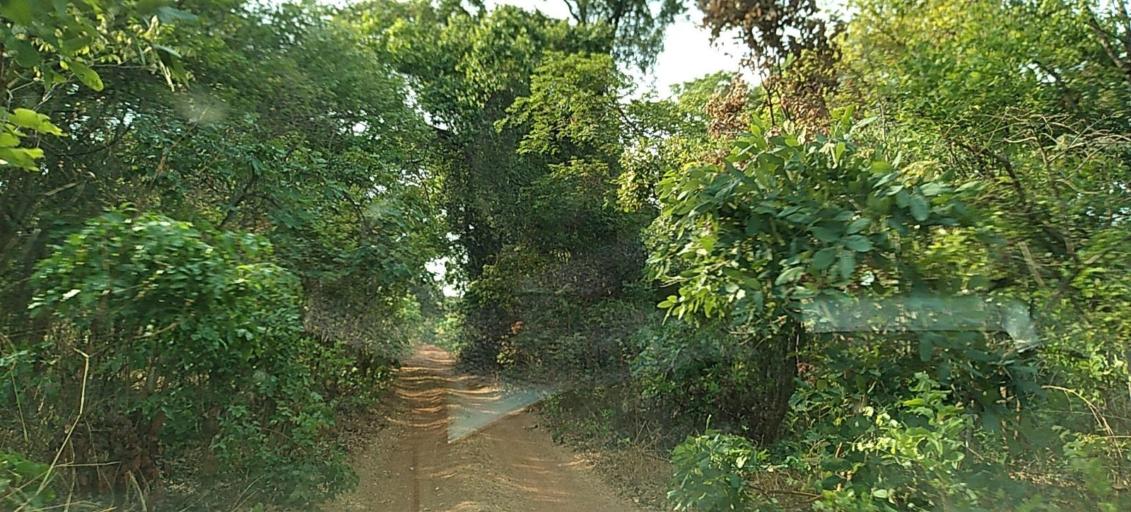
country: ZM
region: Copperbelt
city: Kalulushi
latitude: -12.9772
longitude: 27.7162
